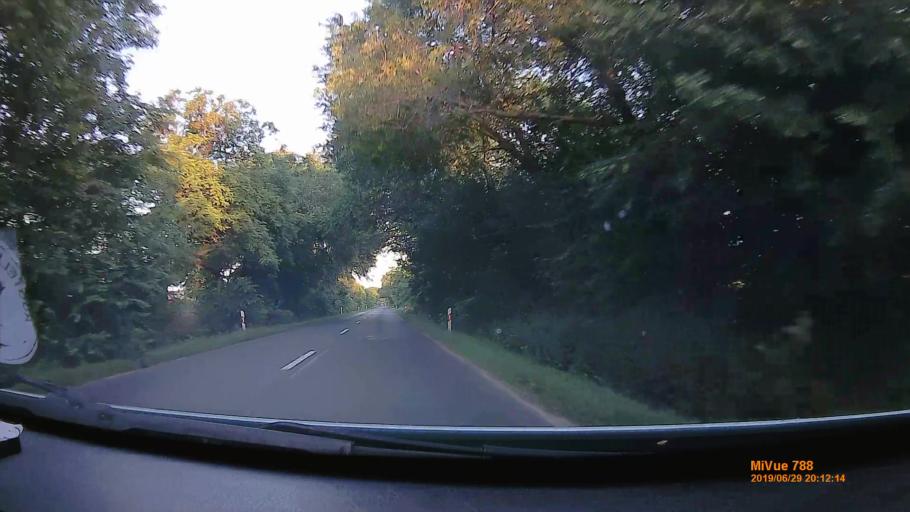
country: HU
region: Pest
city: Paty
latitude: 47.5201
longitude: 18.8025
